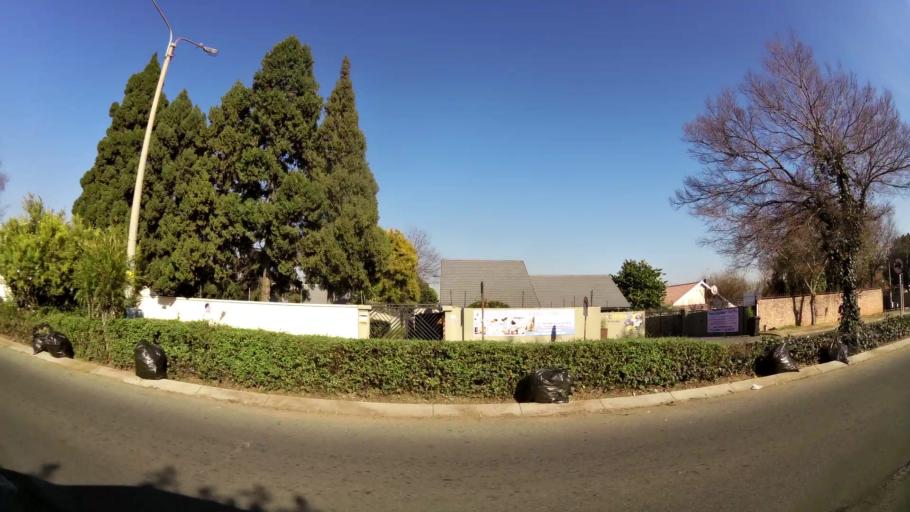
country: ZA
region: Gauteng
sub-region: City of Johannesburg Metropolitan Municipality
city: Modderfontein
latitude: -26.1539
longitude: 28.1529
